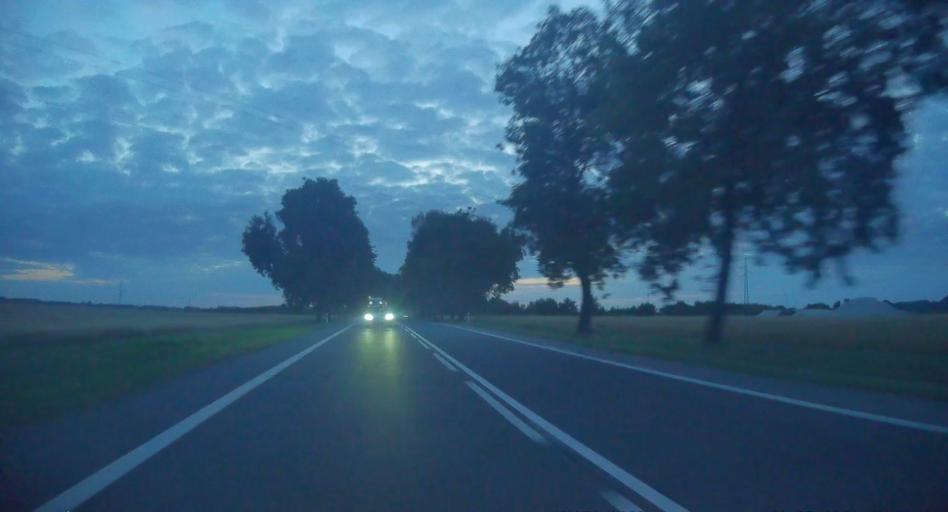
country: PL
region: Silesian Voivodeship
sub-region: Powiat klobucki
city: Klobuck
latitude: 50.9152
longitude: 18.8936
